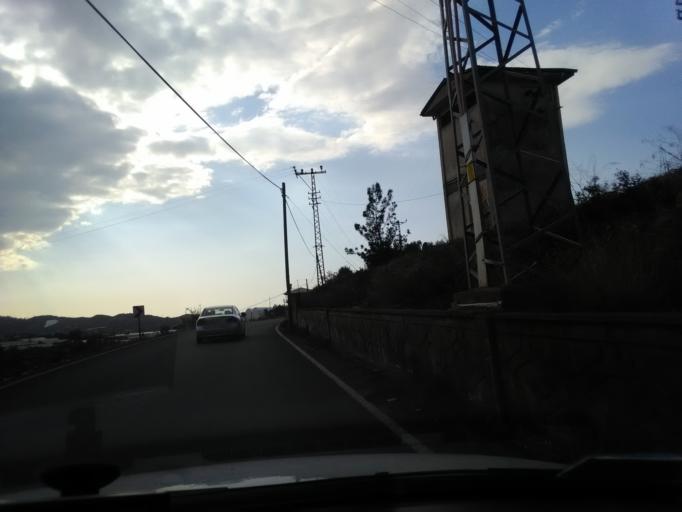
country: TR
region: Antalya
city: Gazipasa
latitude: 36.2751
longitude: 32.3462
